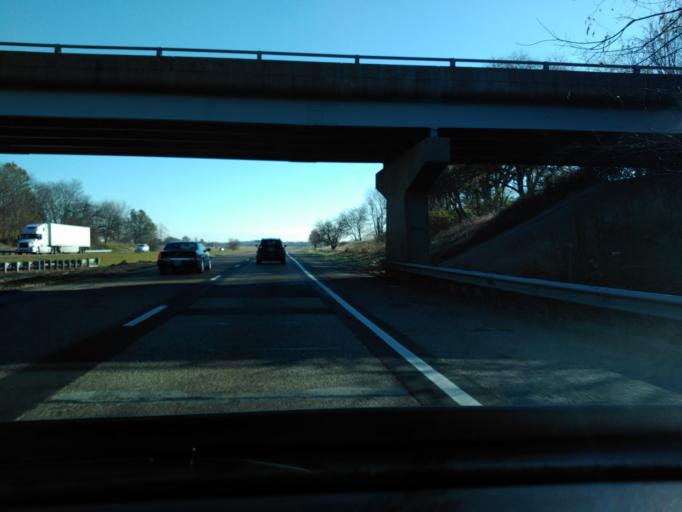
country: US
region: Illinois
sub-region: Madison County
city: Troy
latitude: 38.7555
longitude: -89.8747
